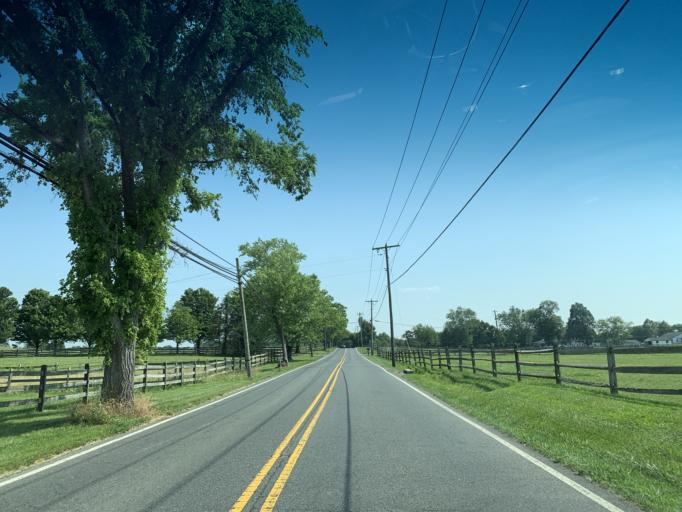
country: US
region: Maryland
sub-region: Montgomery County
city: Poolesville
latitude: 39.1606
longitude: -77.4191
